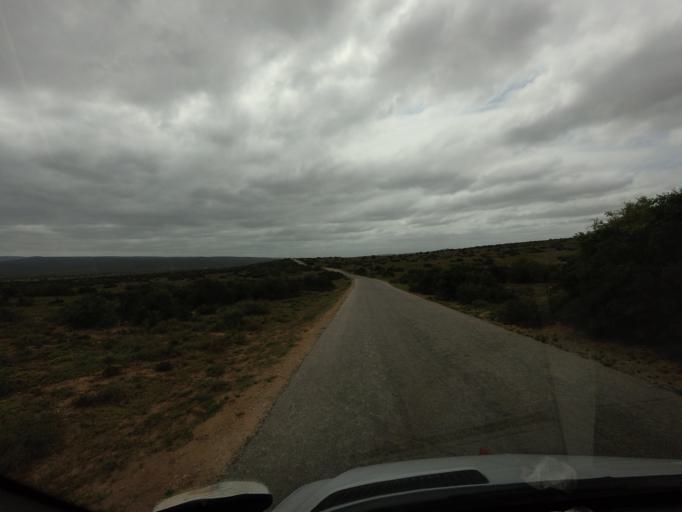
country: ZA
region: Eastern Cape
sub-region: Cacadu District Municipality
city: Kirkwood
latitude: -33.4397
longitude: 25.7706
